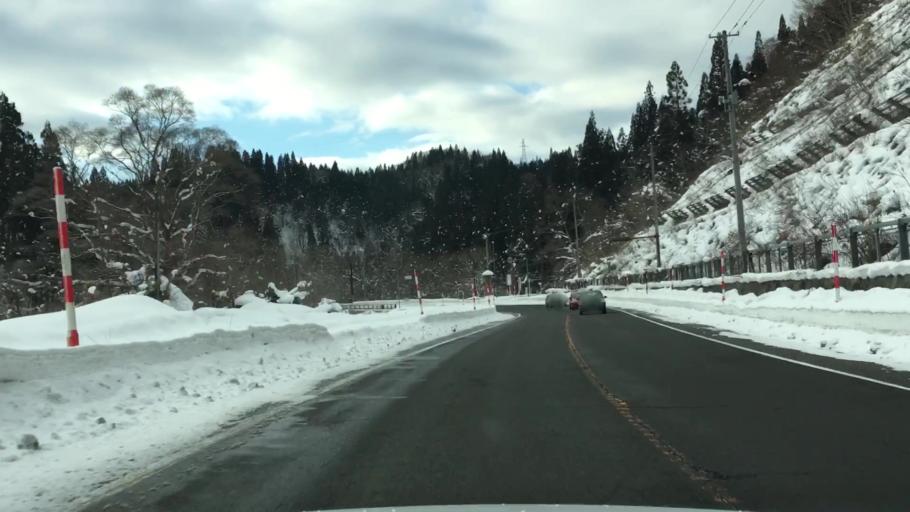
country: JP
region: Akita
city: Odate
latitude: 40.4352
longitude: 140.6355
